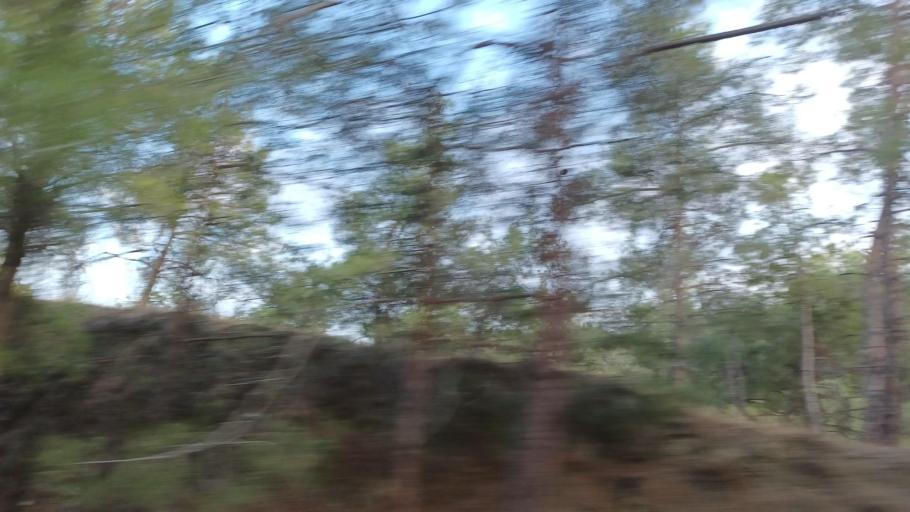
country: CY
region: Lefkosia
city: Kakopetria
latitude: 35.0515
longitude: 32.9079
